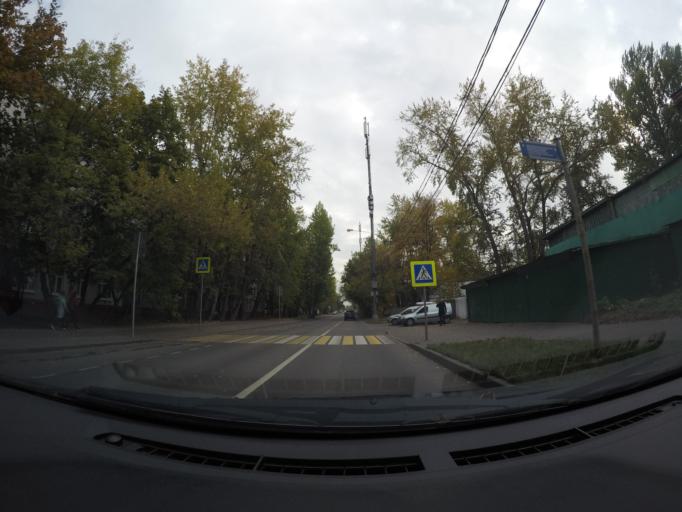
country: RU
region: Moscow
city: Lefortovo
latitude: 55.7629
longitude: 37.7294
